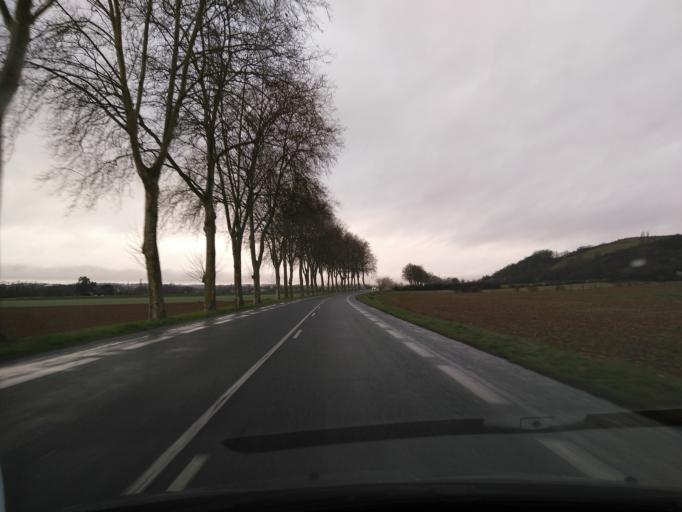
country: FR
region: Midi-Pyrenees
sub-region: Departement de la Haute-Garonne
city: Montesquieu-Volvestre
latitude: 43.2234
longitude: 1.2131
